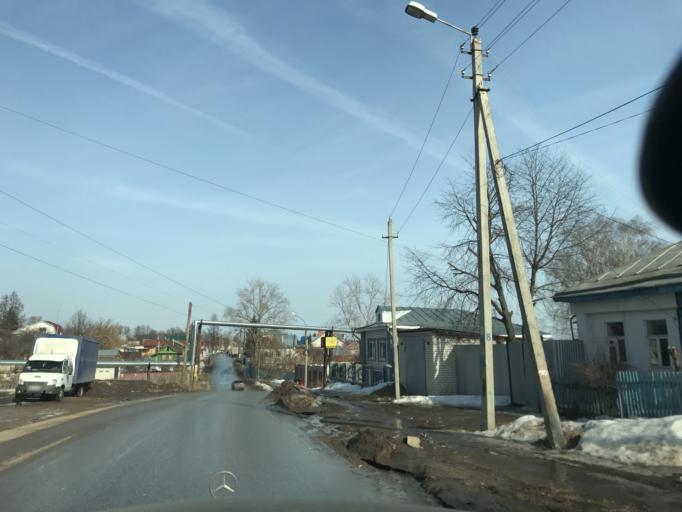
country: RU
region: Nizjnij Novgorod
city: Taremskoye
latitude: 55.9557
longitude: 43.0529
